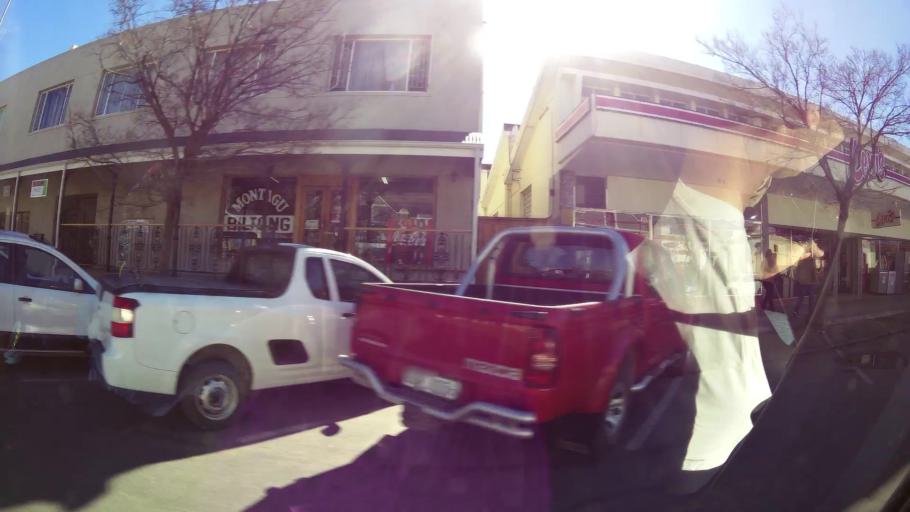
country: ZA
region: Western Cape
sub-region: Cape Winelands District Municipality
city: Ashton
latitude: -33.7869
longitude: 20.1208
